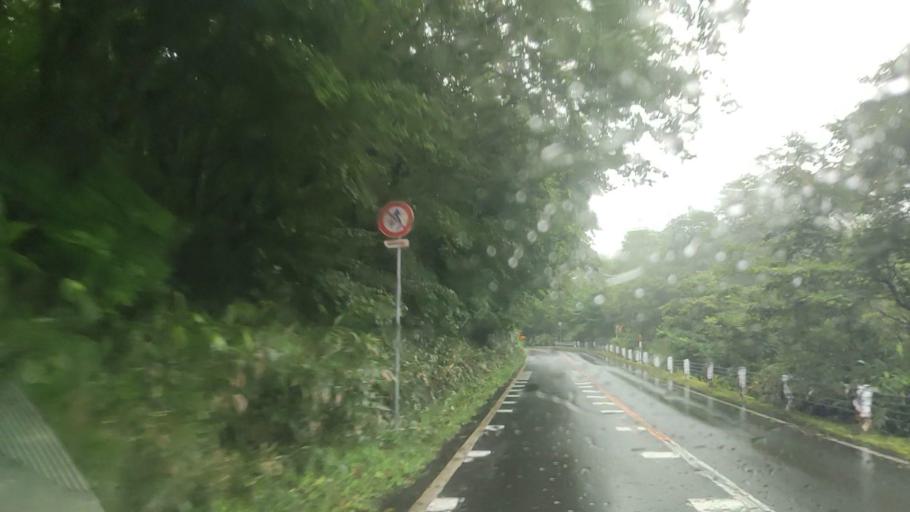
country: JP
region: Hokkaido
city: Muroran
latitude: 42.4950
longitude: 141.1245
